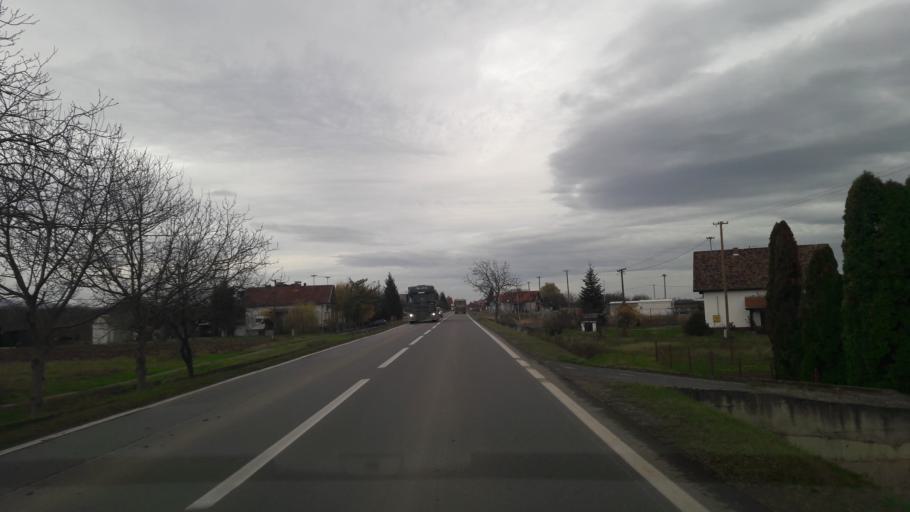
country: HR
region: Osjecko-Baranjska
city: Fericanci
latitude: 45.5265
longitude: 17.9616
